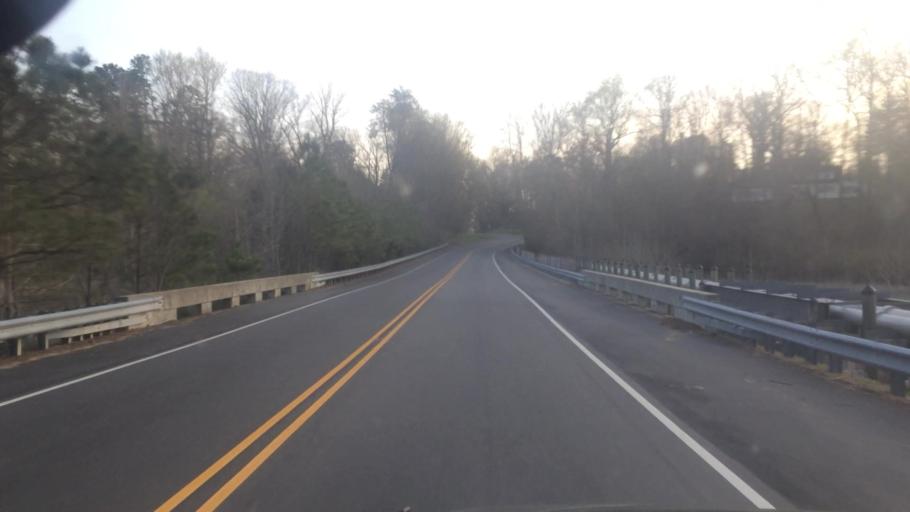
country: US
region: Virginia
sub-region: James City County
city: Williamsburg
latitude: 37.2384
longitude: -76.7469
